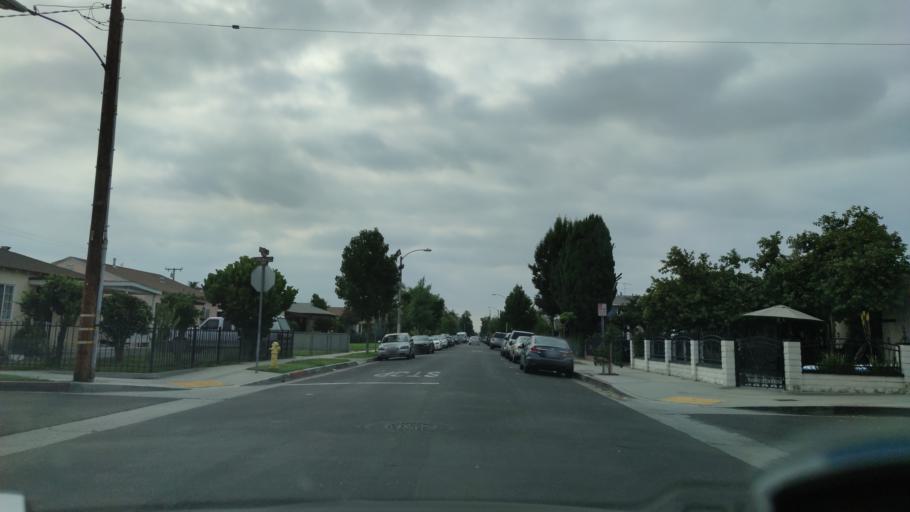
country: US
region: California
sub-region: Los Angeles County
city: Maywood
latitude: 33.9929
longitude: -118.1936
